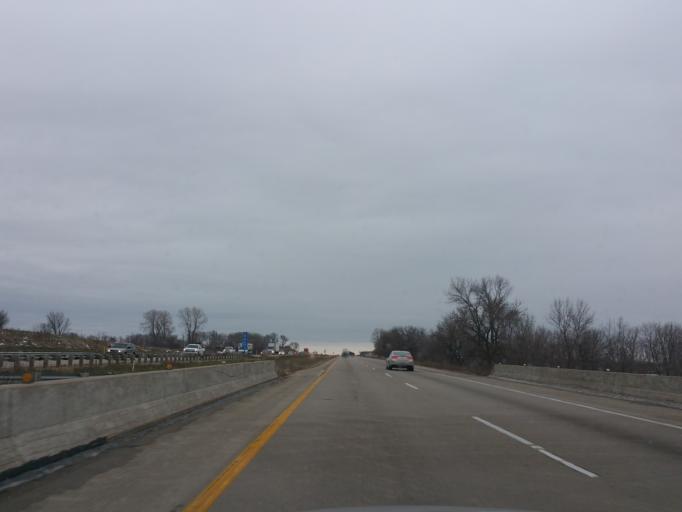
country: US
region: Wisconsin
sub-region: Dane County
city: Deerfield
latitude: 42.9789
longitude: -89.1213
